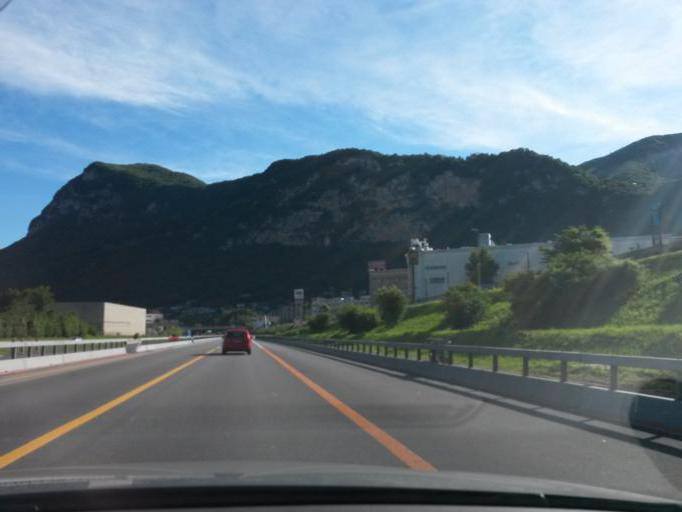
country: CH
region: Ticino
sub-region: Mendrisio District
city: Mendrisio
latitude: 45.8739
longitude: 8.9768
